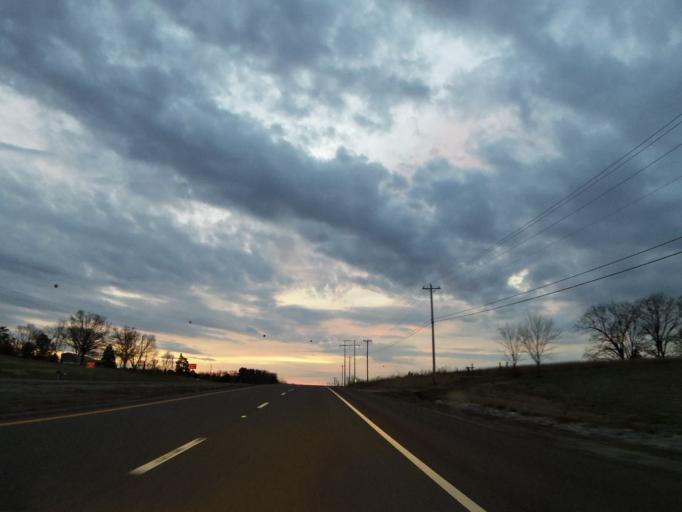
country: US
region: Tennessee
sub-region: Polk County
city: Benton
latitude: 35.2189
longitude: -84.5912
